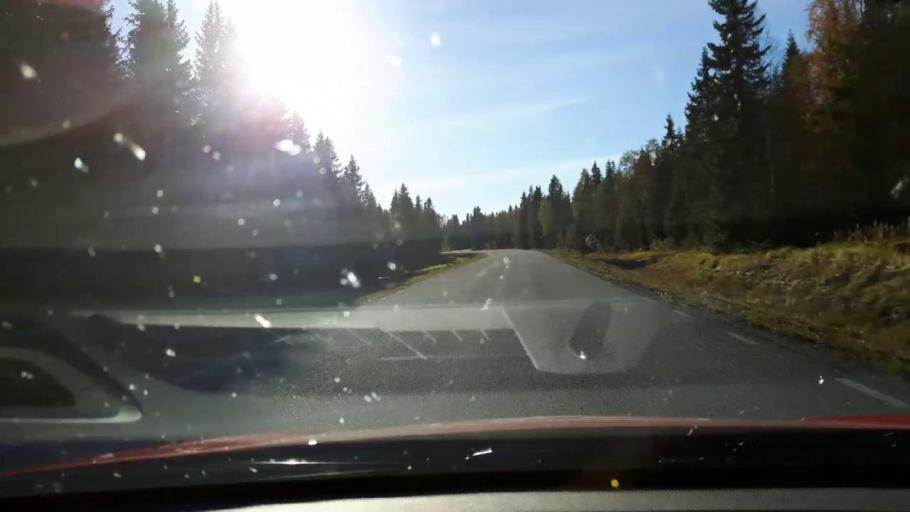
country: SE
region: Jaemtland
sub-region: Stroemsunds Kommun
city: Stroemsund
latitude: 63.8604
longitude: 15.0346
